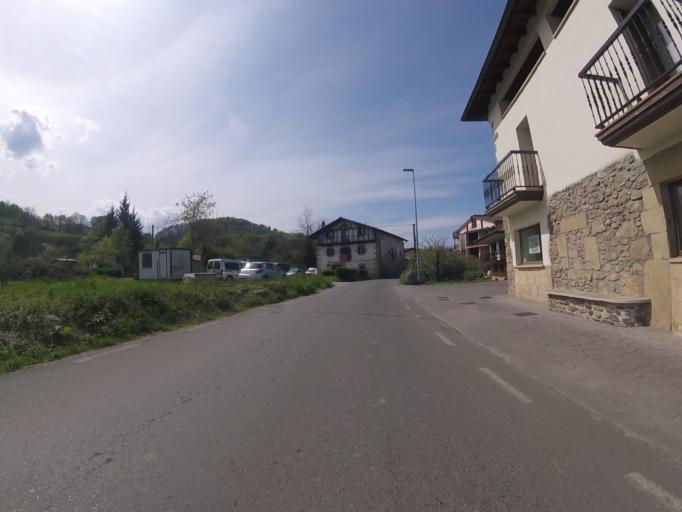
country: ES
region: Basque Country
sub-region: Provincia de Guipuzcoa
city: Lezo
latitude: 43.2929
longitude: -1.8522
